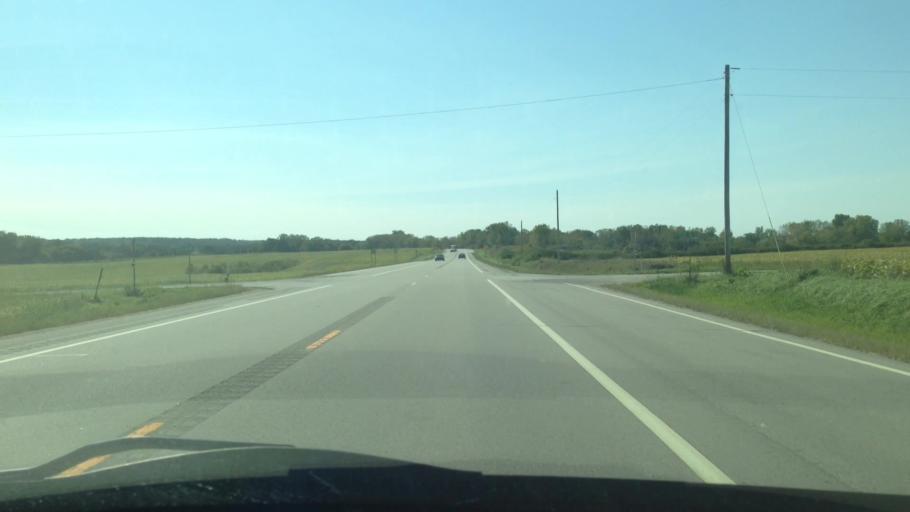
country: US
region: Minnesota
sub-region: Olmsted County
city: Eyota
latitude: 43.9994
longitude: -92.2786
